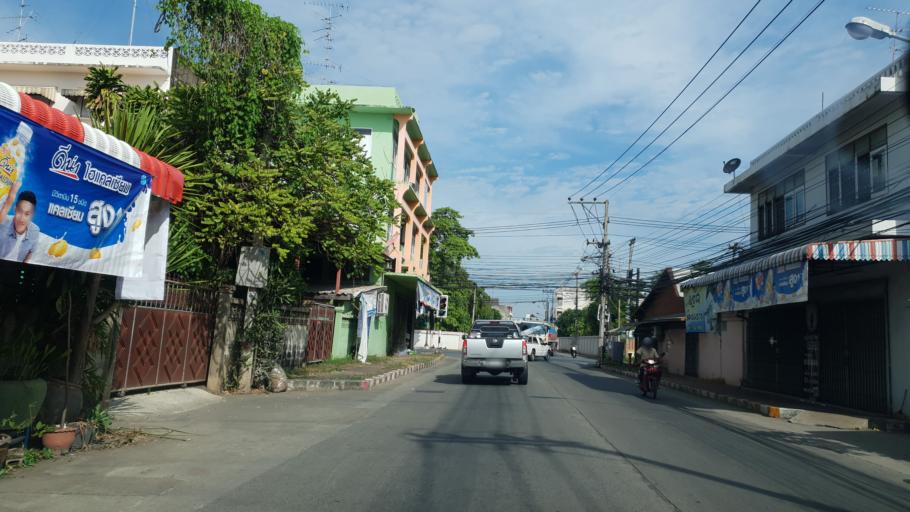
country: TH
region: Phitsanulok
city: Phitsanulok
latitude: 16.8103
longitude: 100.2676
